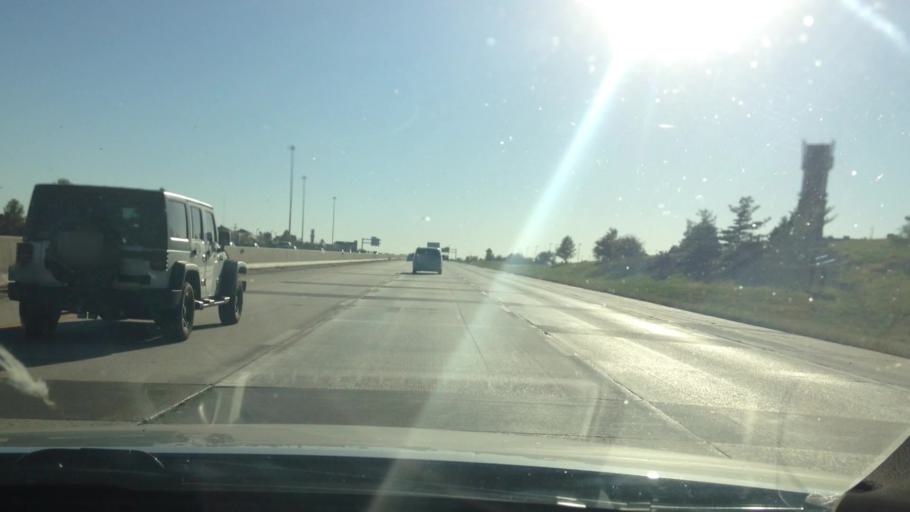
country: US
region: Kansas
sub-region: Johnson County
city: Olathe
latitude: 38.8544
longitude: -94.8169
